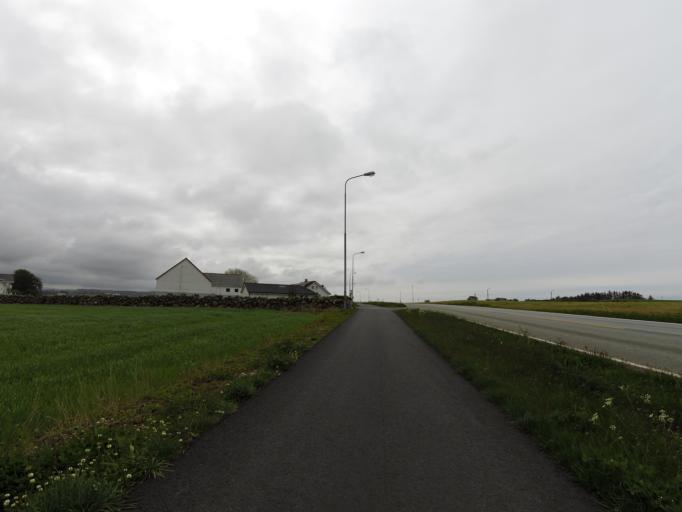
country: NO
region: Rogaland
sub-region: Klepp
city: Kleppe
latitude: 58.8255
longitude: 5.5894
